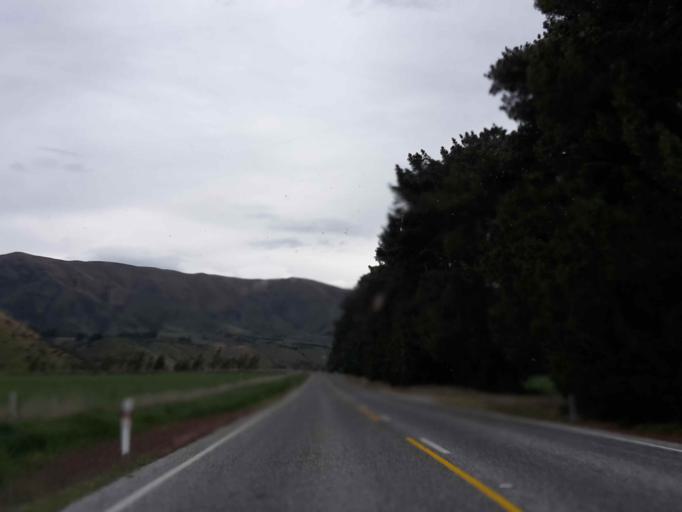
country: NZ
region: Otago
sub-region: Queenstown-Lakes District
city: Wanaka
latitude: -44.7334
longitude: 169.2991
